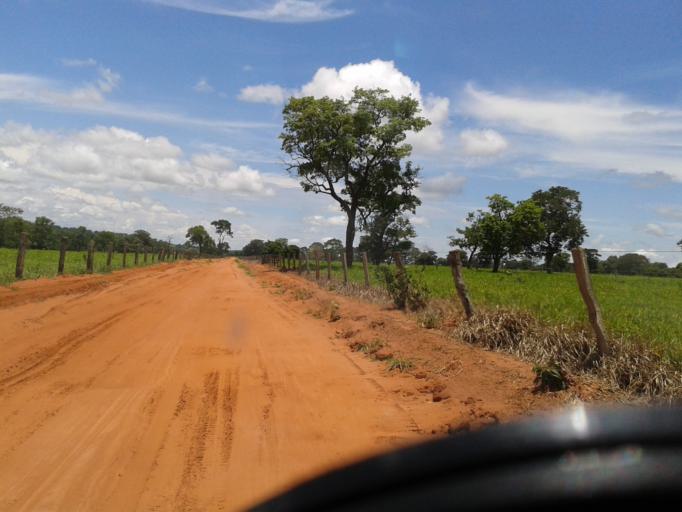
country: BR
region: Minas Gerais
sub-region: Santa Vitoria
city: Santa Vitoria
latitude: -18.9418
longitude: -49.8607
